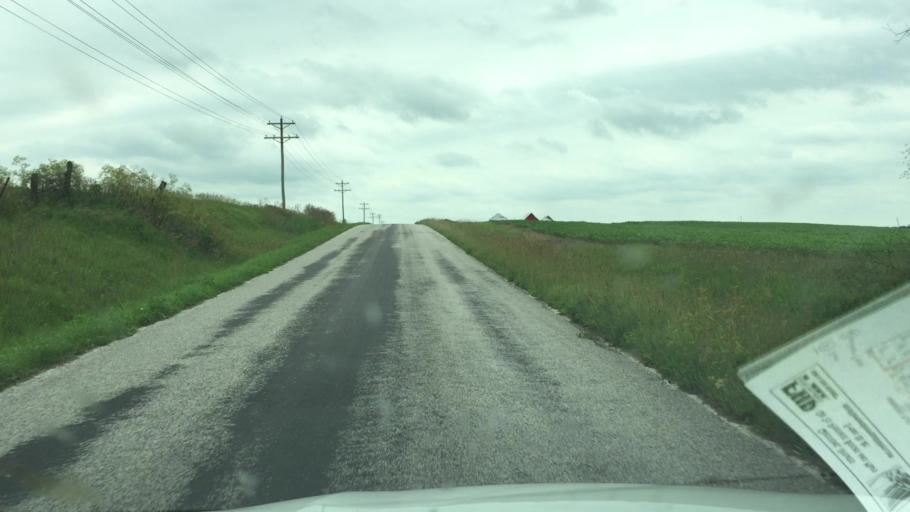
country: US
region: Illinois
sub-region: Hancock County
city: Carthage
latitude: 40.2941
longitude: -91.0833
